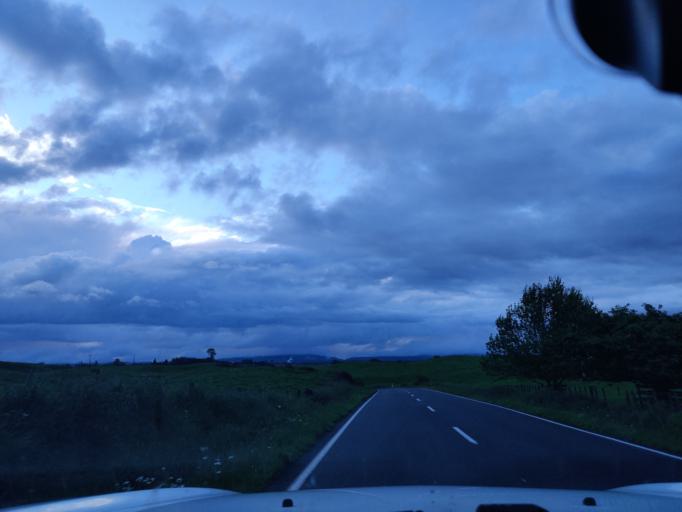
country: NZ
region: Waikato
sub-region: South Waikato District
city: Tokoroa
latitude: -38.2079
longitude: 175.8222
